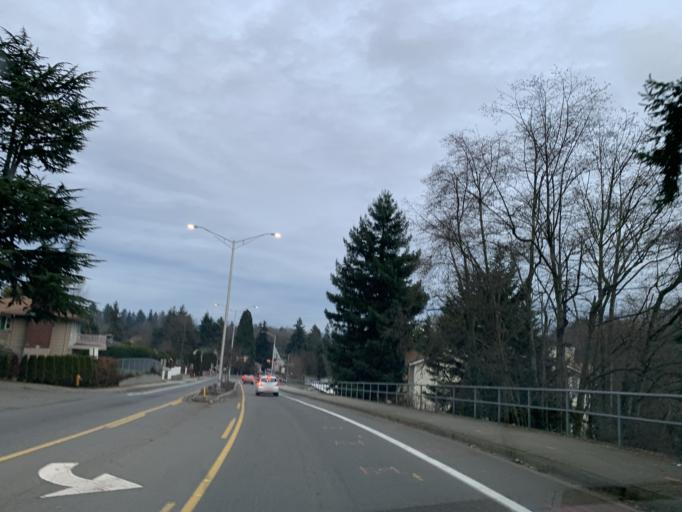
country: US
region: Washington
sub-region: King County
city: SeaTac
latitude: 47.4652
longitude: -122.2834
